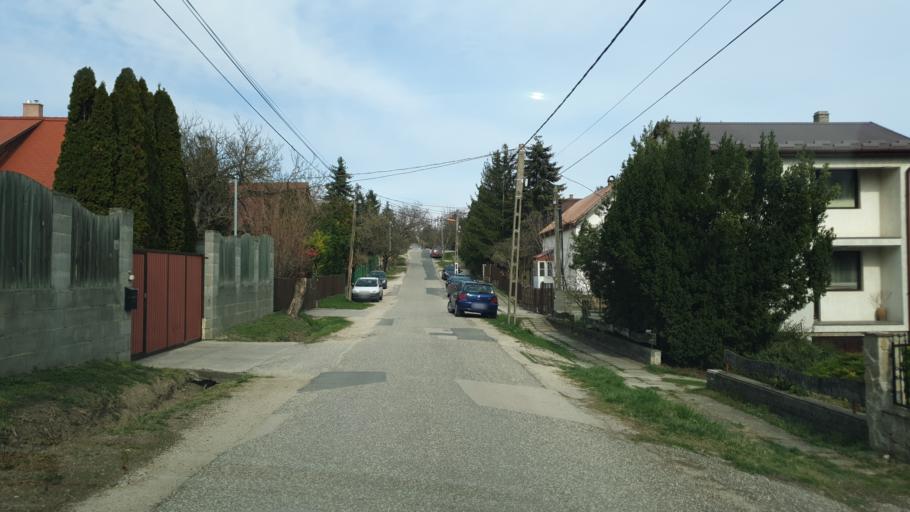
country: HU
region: Pest
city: Biatorbagy
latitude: 47.4681
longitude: 18.8242
